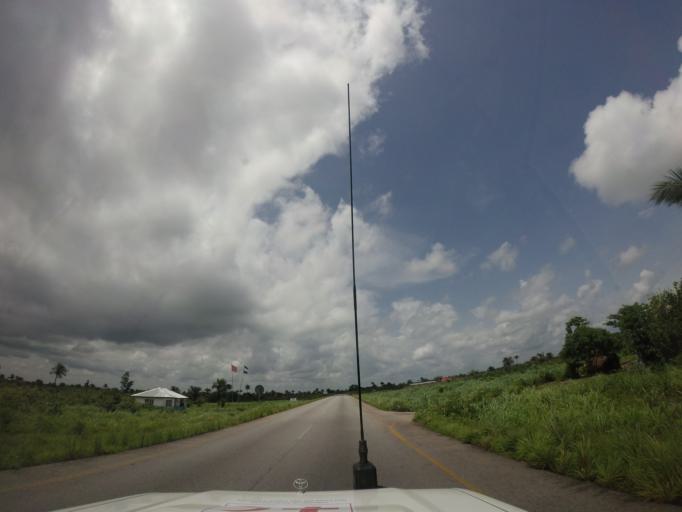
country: SL
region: Northern Province
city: Lunsar
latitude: 8.4748
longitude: -12.5408
